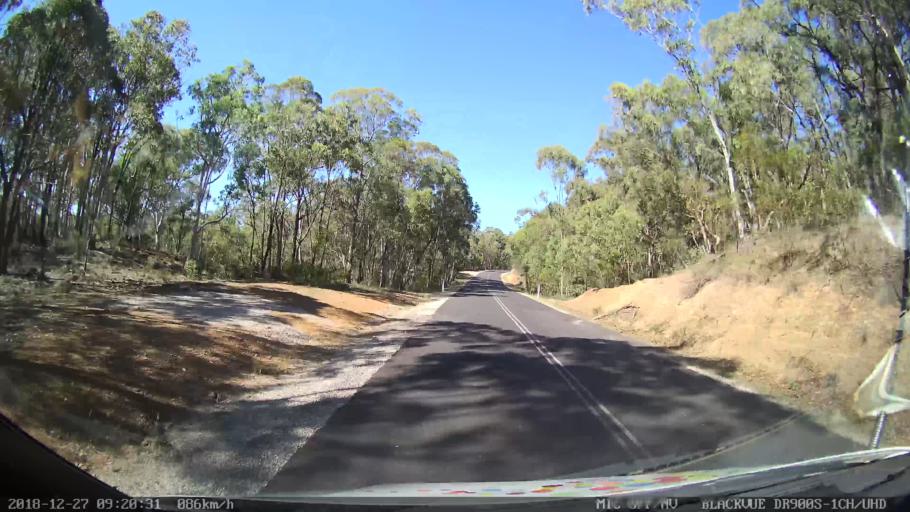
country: AU
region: New South Wales
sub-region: Lithgow
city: Portland
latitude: -33.1202
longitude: 150.0218
